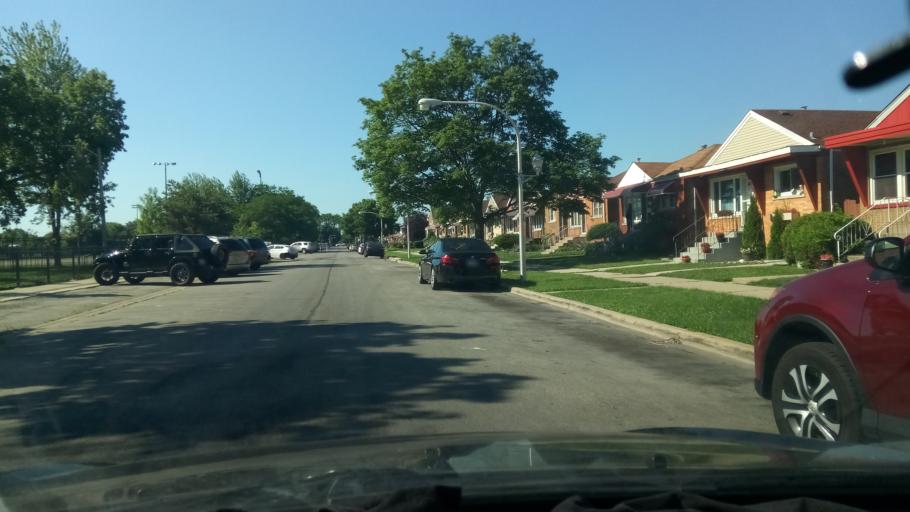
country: US
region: Illinois
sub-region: Cook County
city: Hometown
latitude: 41.7748
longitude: -87.7301
